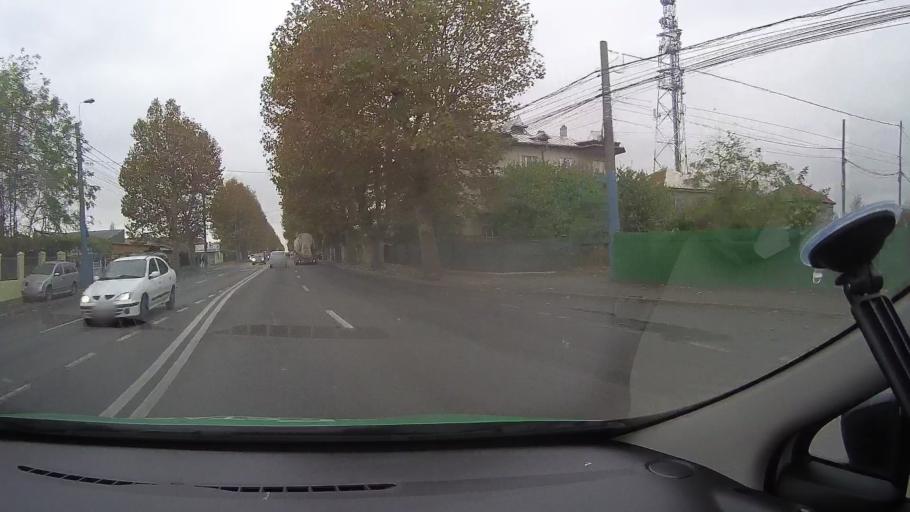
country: RO
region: Constanta
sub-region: Municipiul Constanta
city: Constanta
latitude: 44.1693
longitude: 28.5863
